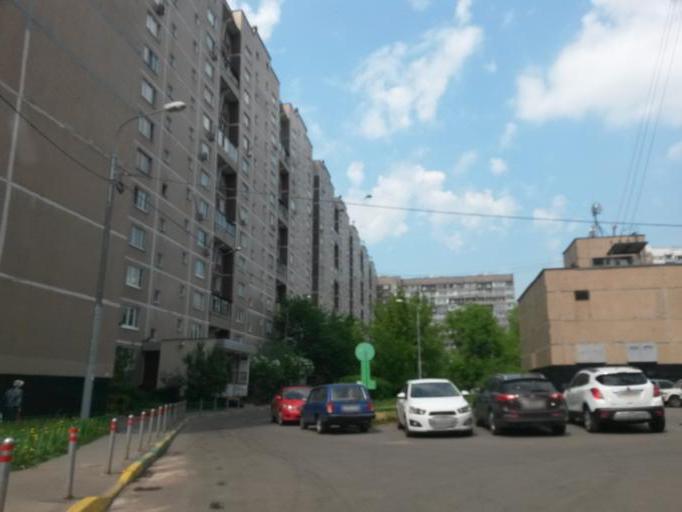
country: RU
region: Moscow
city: Mar'ino
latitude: 55.6506
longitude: 37.7384
